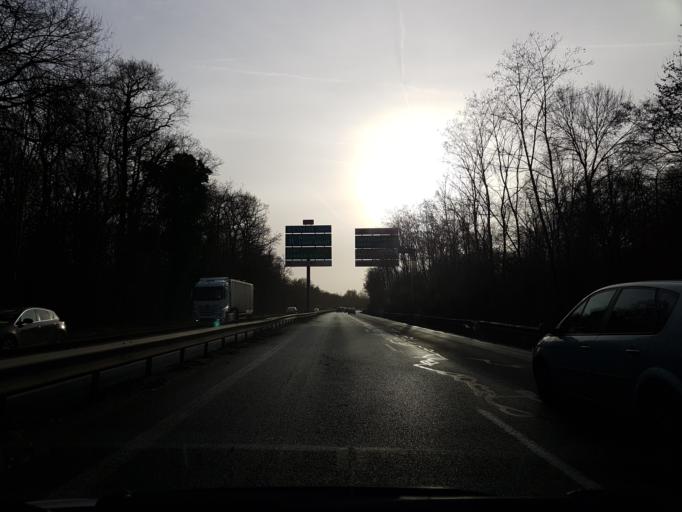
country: FR
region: Ile-de-France
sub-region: Departement de l'Essonne
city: Quincy-sous-Senart
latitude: 48.6504
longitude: 2.5299
